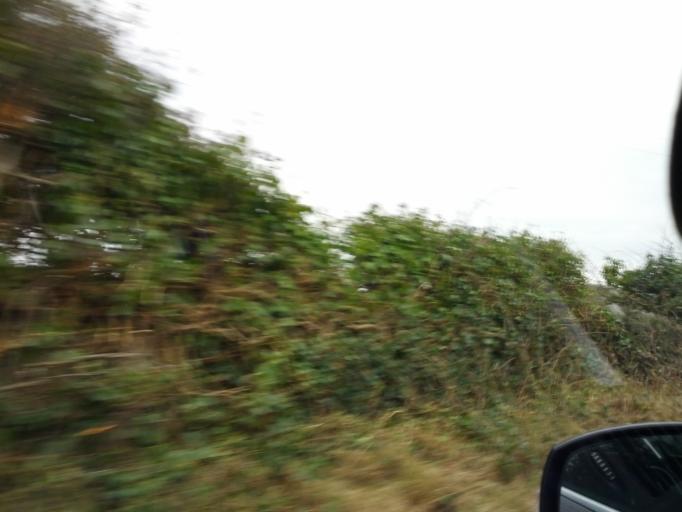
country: IE
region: Connaught
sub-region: County Galway
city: Oranmore
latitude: 53.1808
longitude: -8.9046
